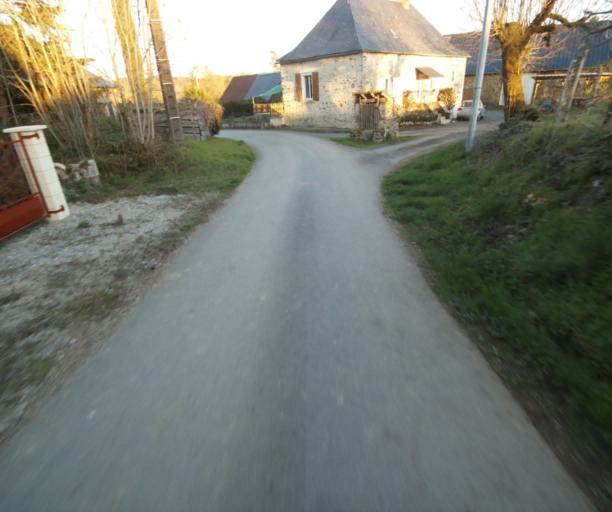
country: FR
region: Limousin
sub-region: Departement de la Correze
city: Saint-Mexant
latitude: 45.2935
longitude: 1.6060
